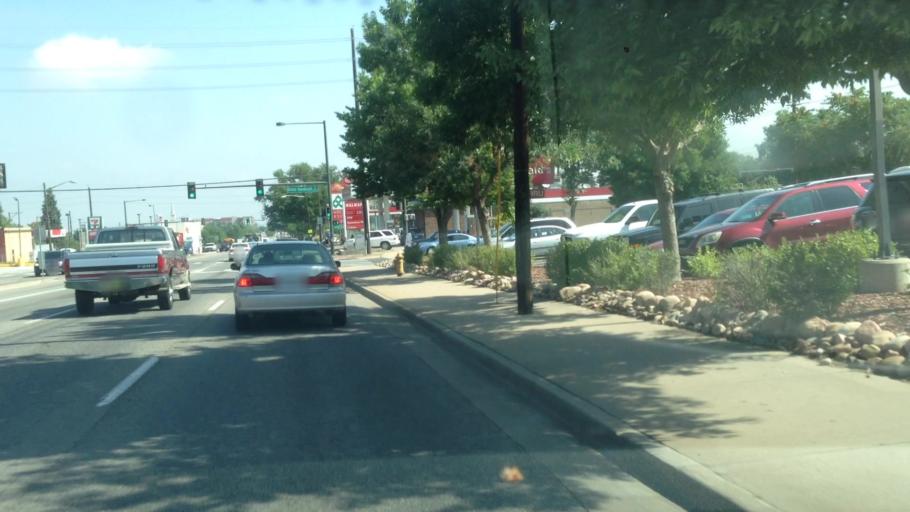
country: US
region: Colorado
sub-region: Adams County
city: Commerce City
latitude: 39.7638
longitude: -104.9405
